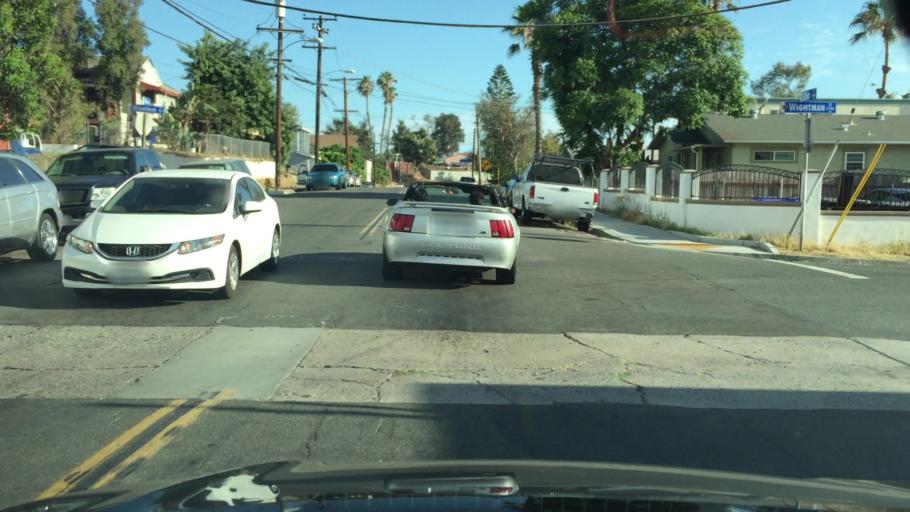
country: US
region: California
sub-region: San Diego County
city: Lemon Grove
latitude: 32.7477
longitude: -117.0837
